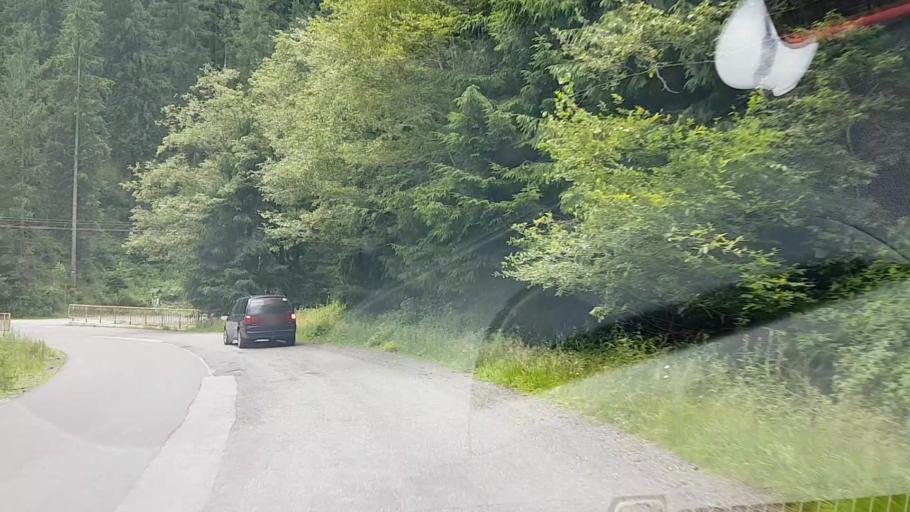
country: RO
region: Suceava
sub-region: Comuna Crucea
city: Crucea
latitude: 47.3506
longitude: 25.6044
